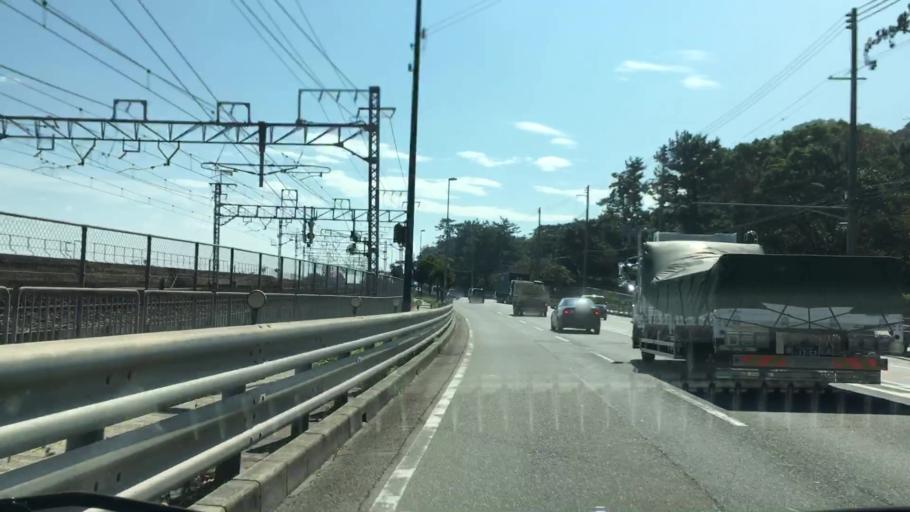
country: JP
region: Hyogo
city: Kobe
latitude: 34.6402
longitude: 135.1054
